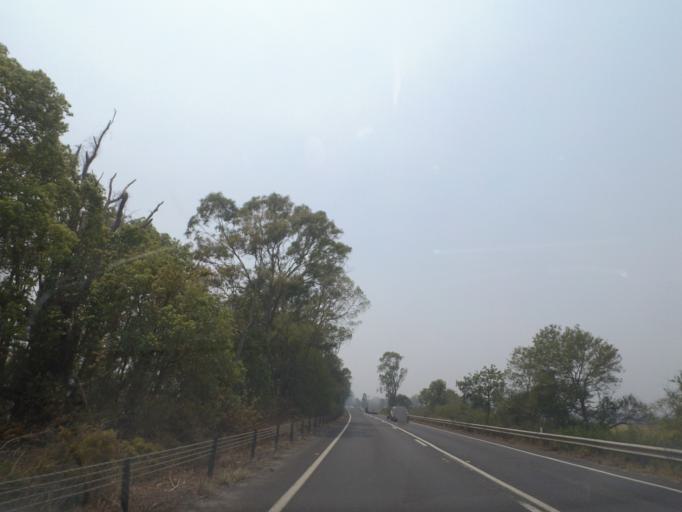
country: AU
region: New South Wales
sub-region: Clarence Valley
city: Maclean
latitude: -29.5418
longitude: 153.1680
